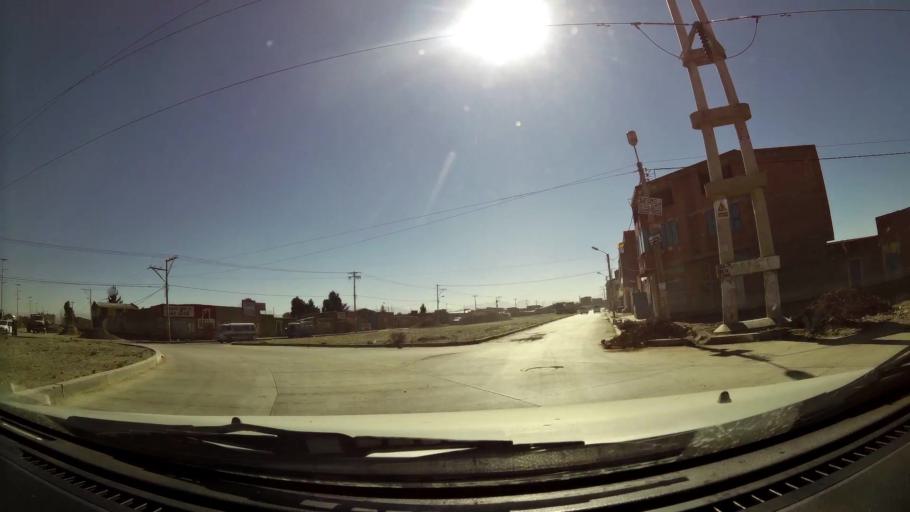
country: BO
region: La Paz
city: La Paz
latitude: -16.5393
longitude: -68.2267
